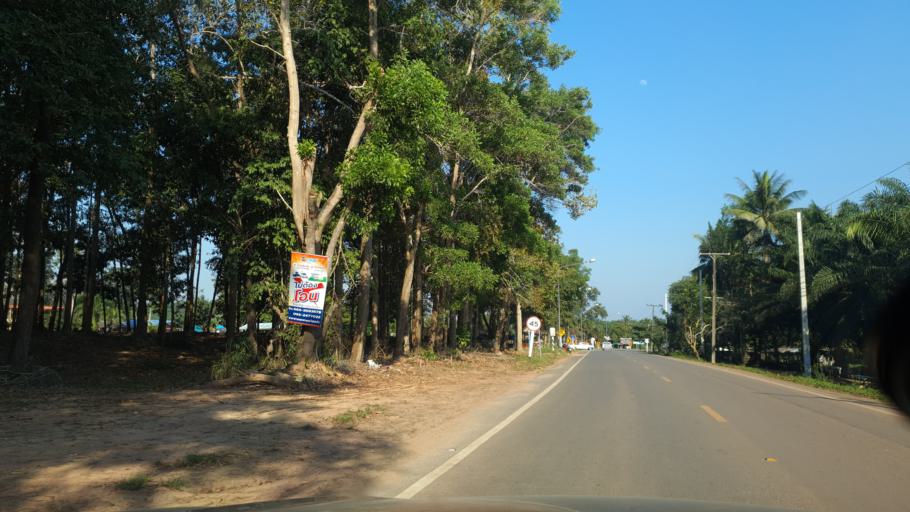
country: TH
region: Chumphon
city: Pathio
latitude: 10.7489
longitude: 99.3317
